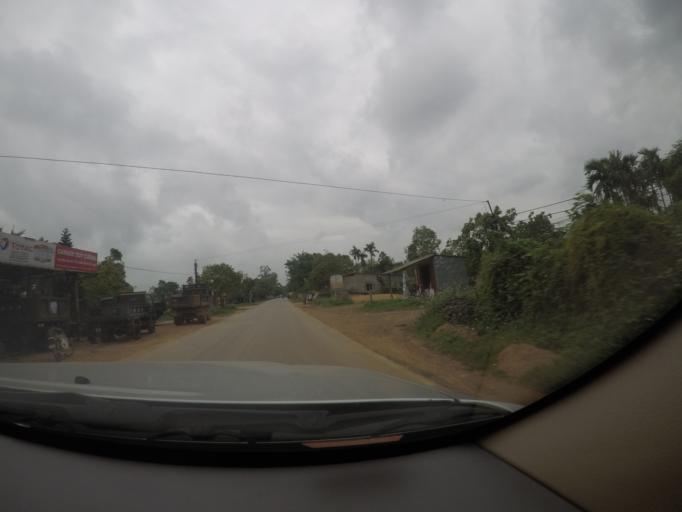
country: VN
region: Quang Tri
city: Cam Lo
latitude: 16.8854
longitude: 106.9927
